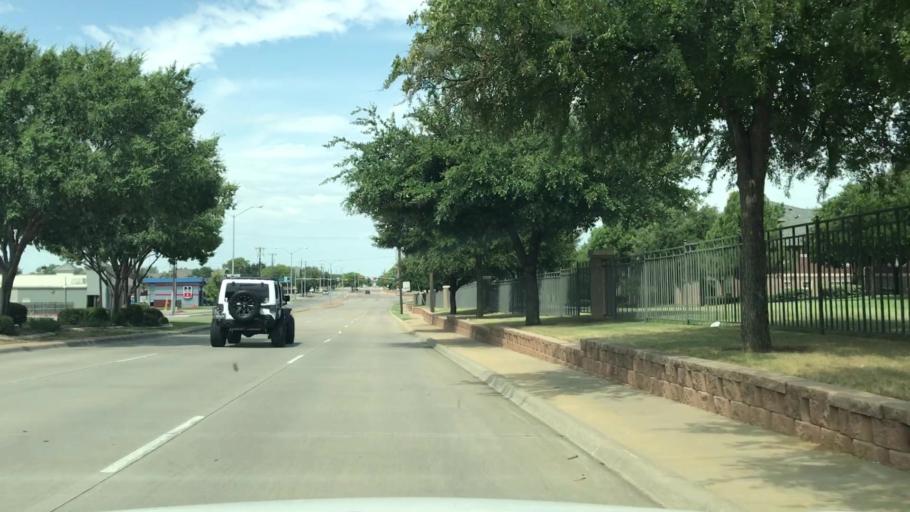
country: US
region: Texas
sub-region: Tarrant County
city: Euless
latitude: 32.8518
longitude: -97.0699
